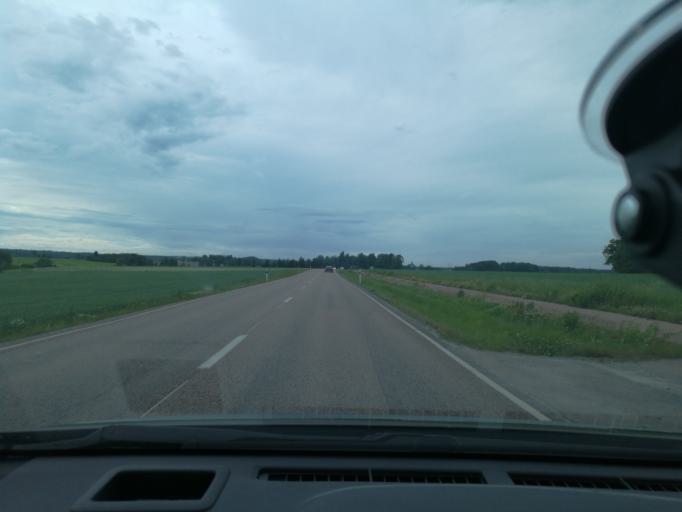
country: SE
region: Vaestmanland
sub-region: Vasteras
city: Skultuna
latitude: 59.6879
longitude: 16.4477
